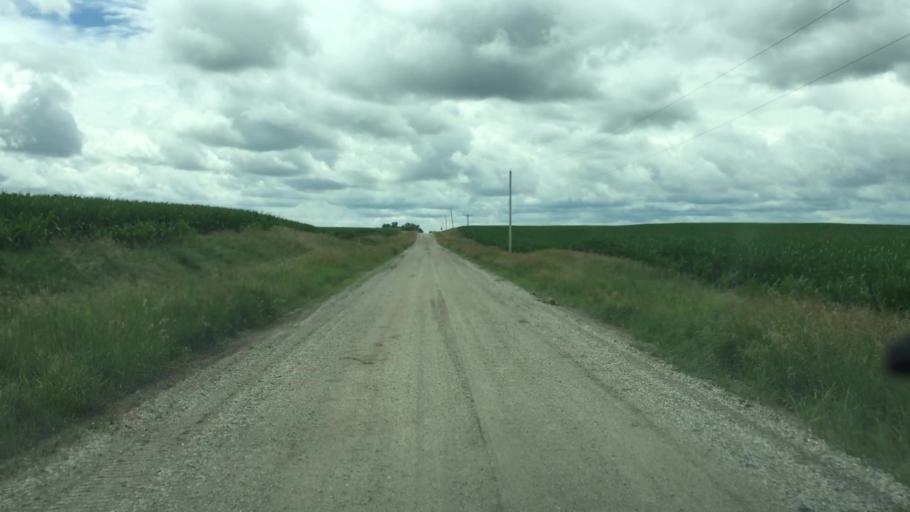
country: US
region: Iowa
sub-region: Jasper County
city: Prairie City
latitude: 41.5861
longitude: -93.1596
